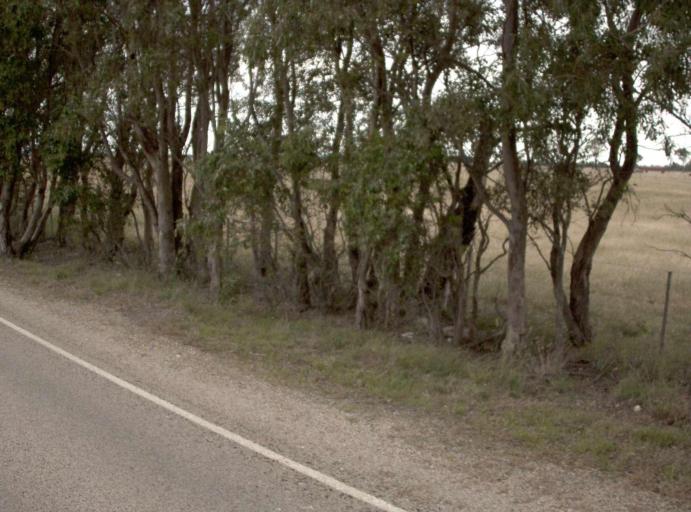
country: AU
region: Victoria
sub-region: East Gippsland
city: Bairnsdale
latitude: -37.8974
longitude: 147.5543
